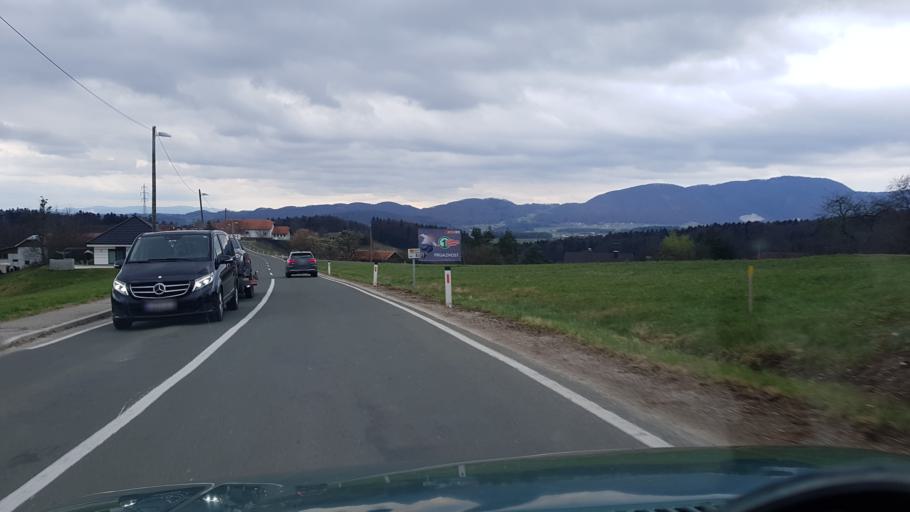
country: SI
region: Oplotnica
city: Oplotnica
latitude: 46.3657
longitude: 15.5011
